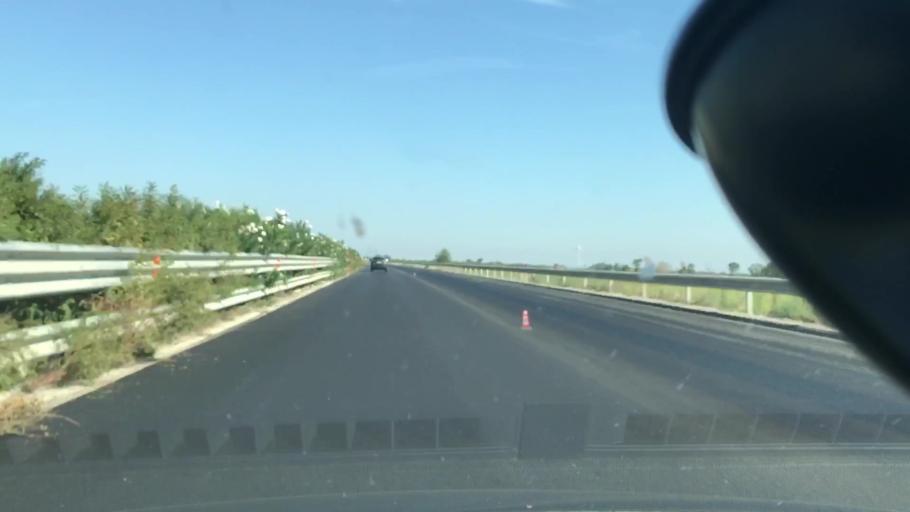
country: IT
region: Apulia
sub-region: Provincia di Foggia
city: Ascoli Satriano
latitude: 41.2761
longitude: 15.5536
